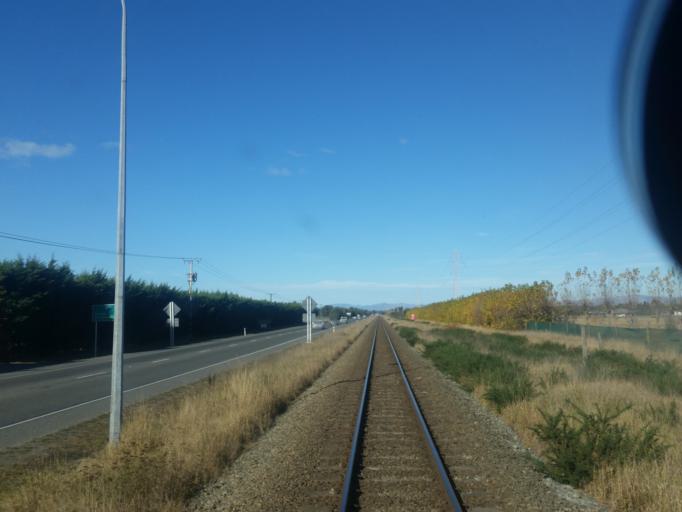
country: NZ
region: Canterbury
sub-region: Waimakariri District
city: Kaiapoi
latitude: -43.3326
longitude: 172.6055
